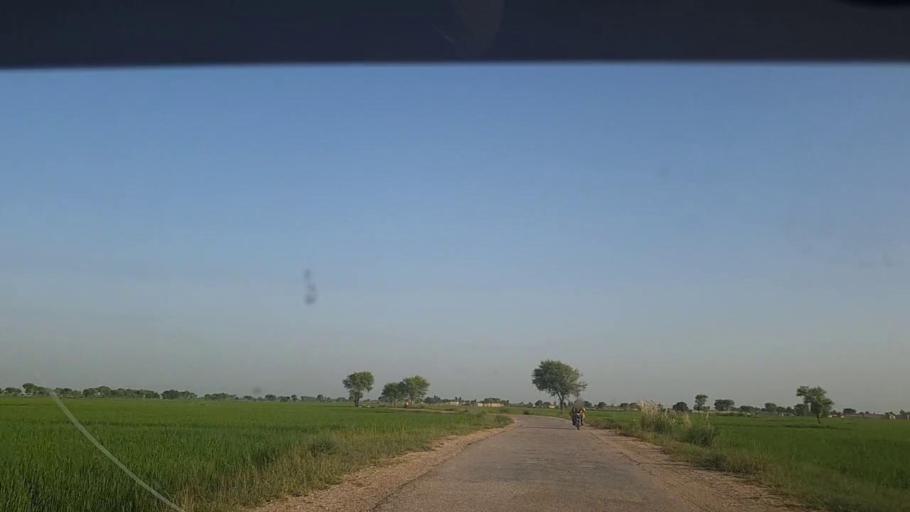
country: PK
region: Sindh
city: Thul
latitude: 28.1365
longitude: 68.8875
